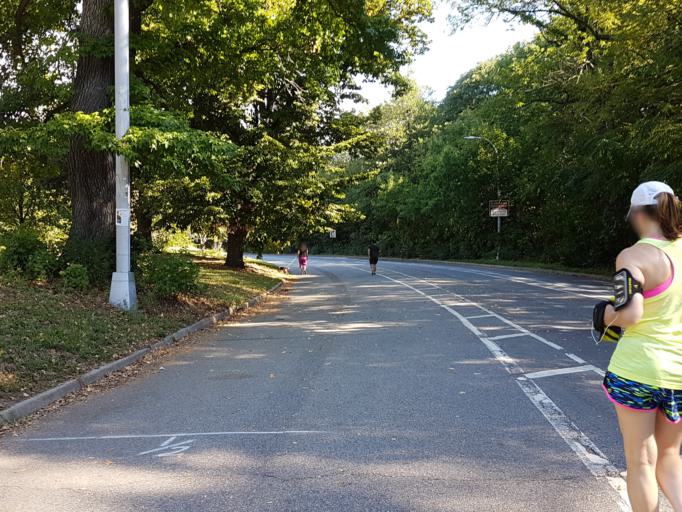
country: US
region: New York
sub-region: Kings County
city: Brooklyn
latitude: 40.6697
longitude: -73.9689
